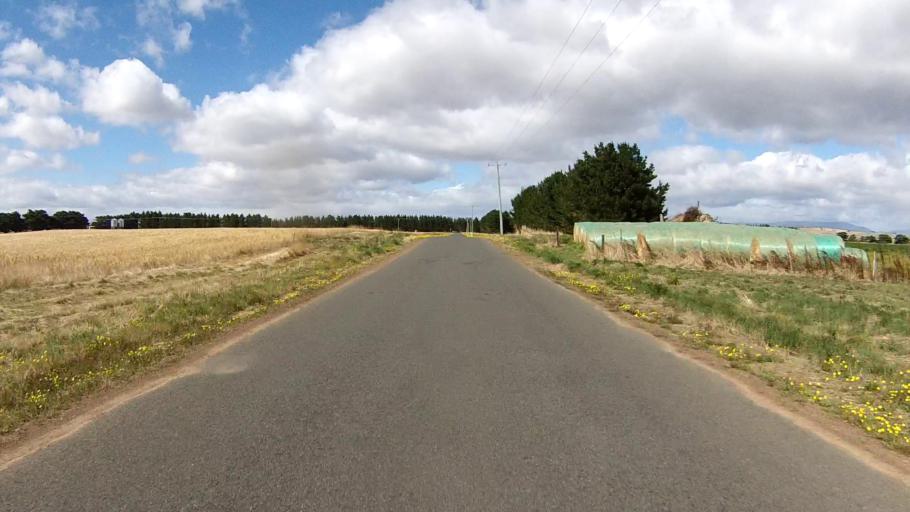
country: AU
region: Tasmania
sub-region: Northern Midlands
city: Evandale
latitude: -41.7738
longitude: 147.4747
